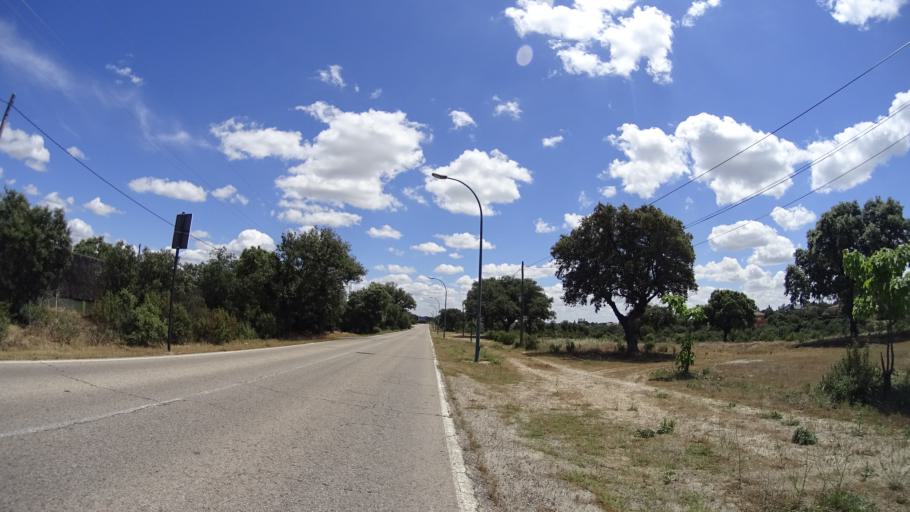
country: ES
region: Madrid
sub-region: Provincia de Madrid
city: Brunete
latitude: 40.4216
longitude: -3.9678
